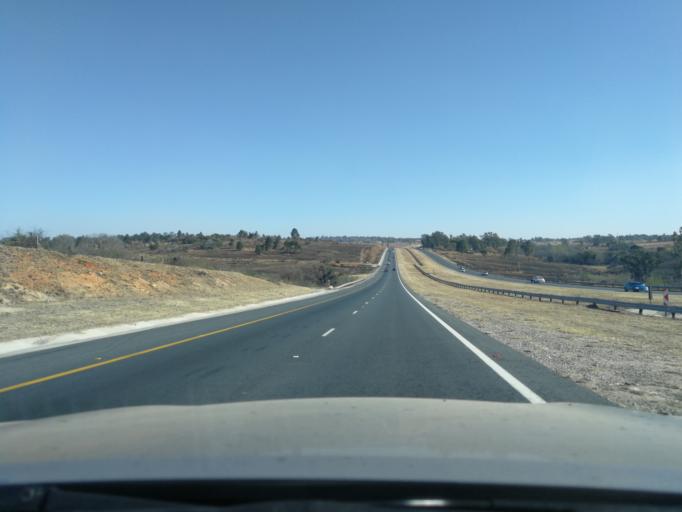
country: ZA
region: Gauteng
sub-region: West Rand District Municipality
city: Muldersdriseloop
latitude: -25.9974
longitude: 27.9069
